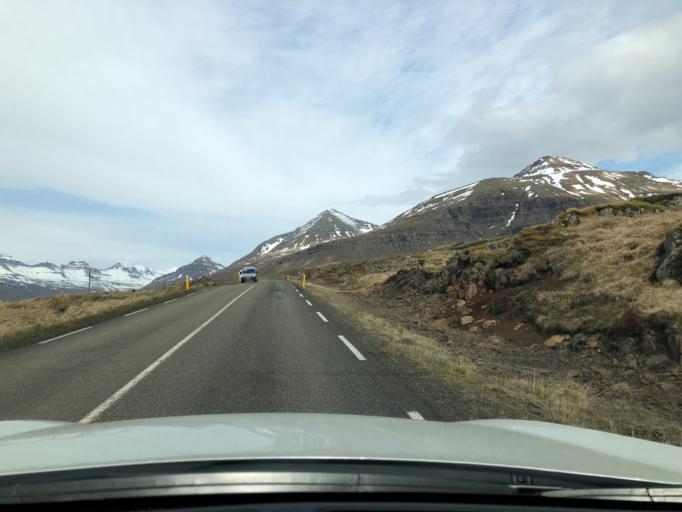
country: IS
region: East
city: Eskifjoerdur
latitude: 64.8289
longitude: -13.8443
